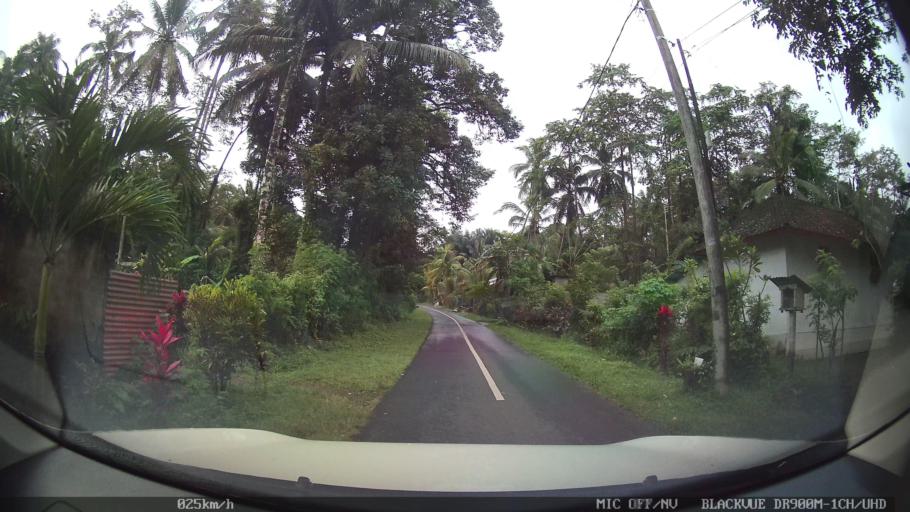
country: ID
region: Bali
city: Pegongan
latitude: -8.4802
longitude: 115.2297
